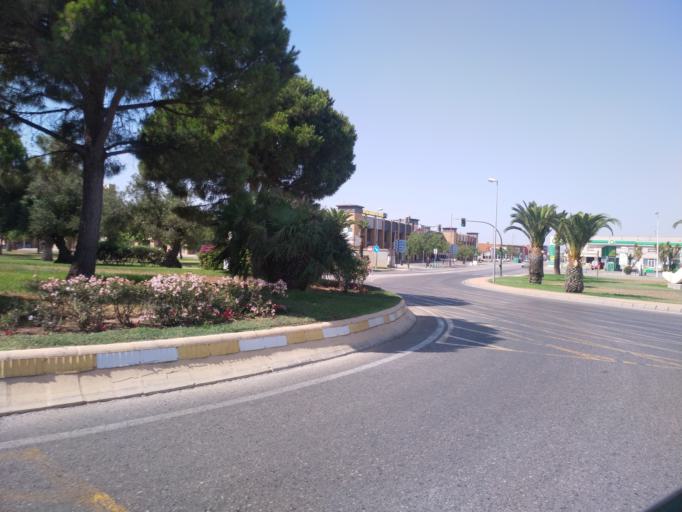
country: ES
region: Andalusia
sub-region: Provincia de Cadiz
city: Chiclana de la Frontera
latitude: 36.4246
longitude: -6.1536
